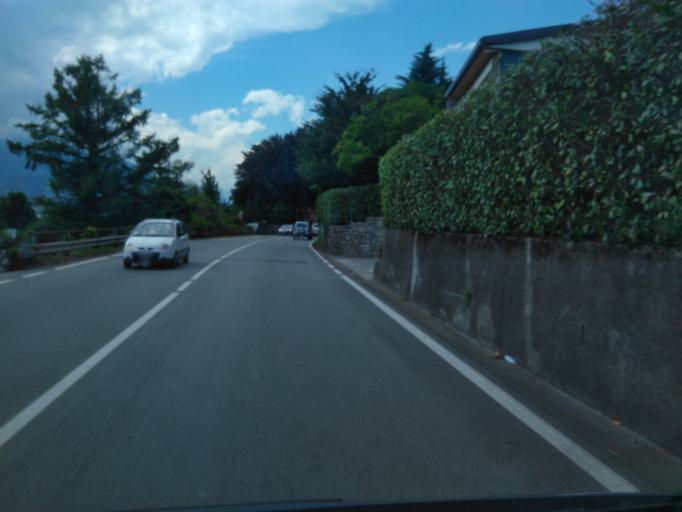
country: IT
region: Piedmont
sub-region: Provincia Verbano-Cusio-Ossola
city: Santino
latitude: 45.9351
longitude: 8.5255
